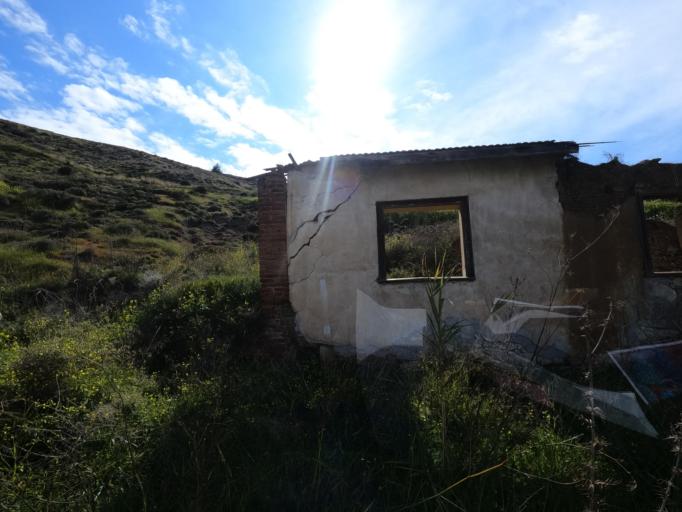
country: CY
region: Lefkosia
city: Lefka
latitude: 35.1017
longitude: 32.8866
